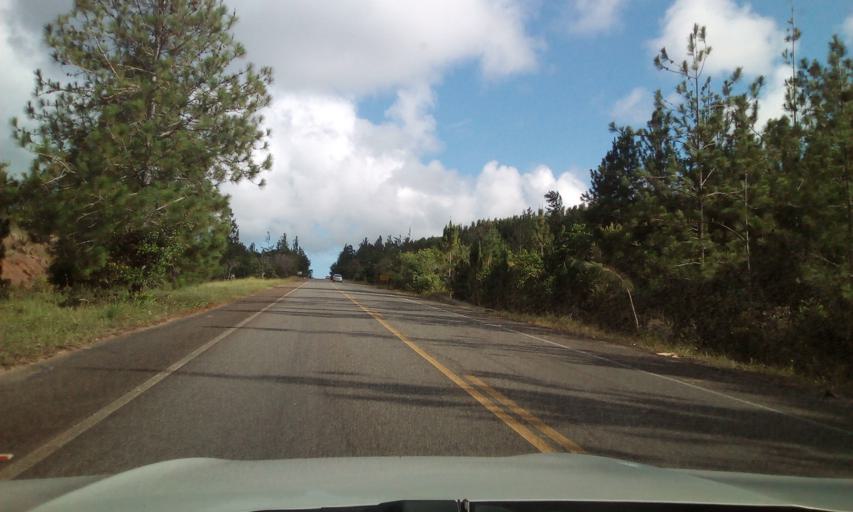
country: BR
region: Bahia
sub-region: Entre Rios
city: Entre Rios
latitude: -12.1375
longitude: -37.7915
